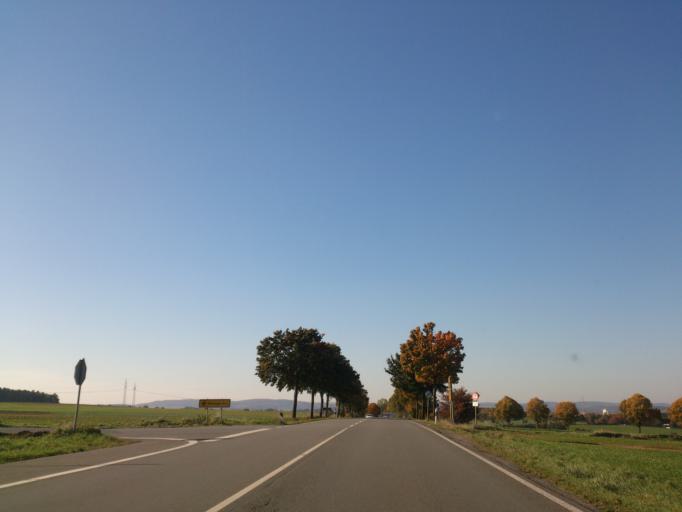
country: DE
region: North Rhine-Westphalia
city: Warburg
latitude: 51.4696
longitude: 9.1924
